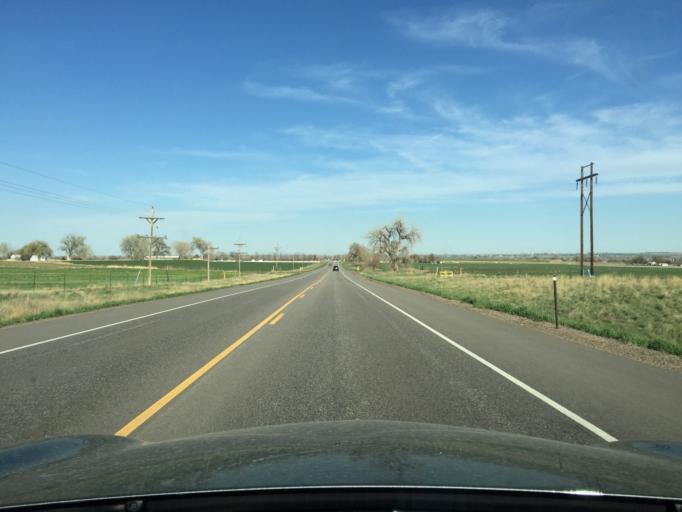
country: US
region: Colorado
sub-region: Boulder County
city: Niwot
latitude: 40.0873
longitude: -105.1153
